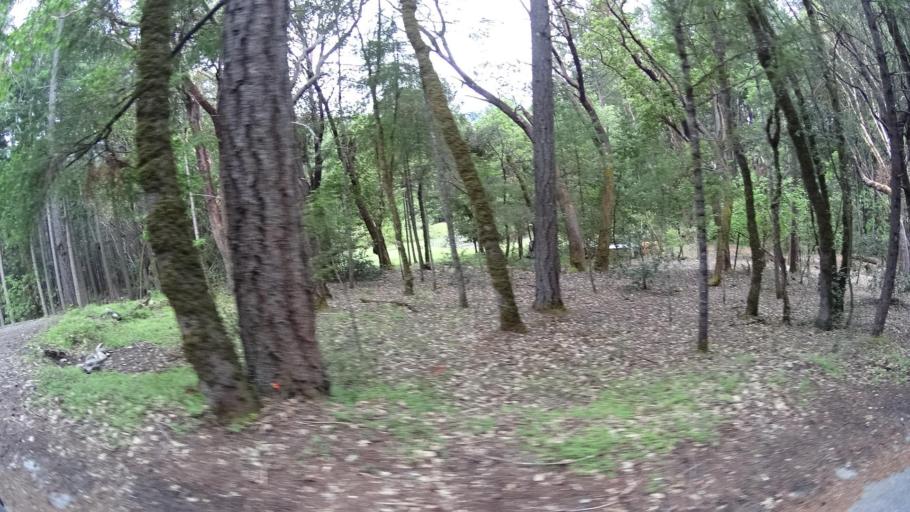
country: US
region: California
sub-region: Humboldt County
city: Willow Creek
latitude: 40.9306
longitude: -123.6159
